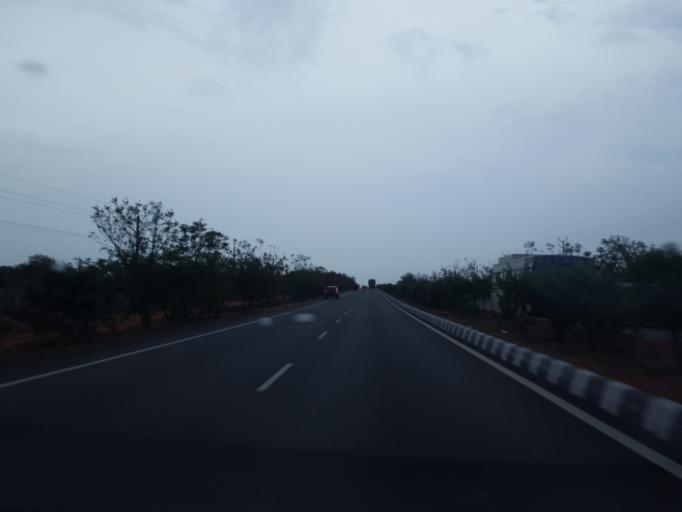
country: IN
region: Telangana
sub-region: Mahbubnagar
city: Farrukhnagar
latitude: 17.1222
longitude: 78.2735
